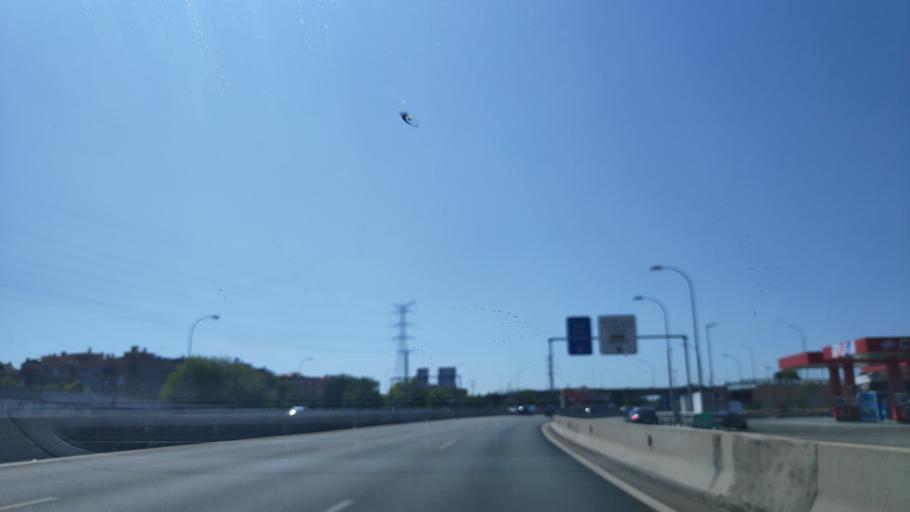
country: ES
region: Madrid
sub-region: Provincia de Madrid
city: Getafe
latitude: 40.3298
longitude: -3.7254
